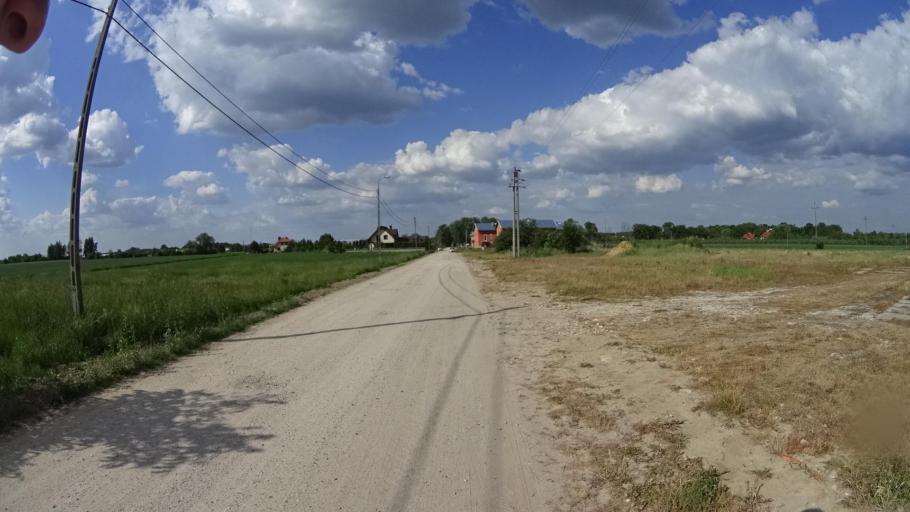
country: PL
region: Masovian Voivodeship
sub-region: Powiat piaseczynski
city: Tarczyn
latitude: 52.0293
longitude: 20.8201
